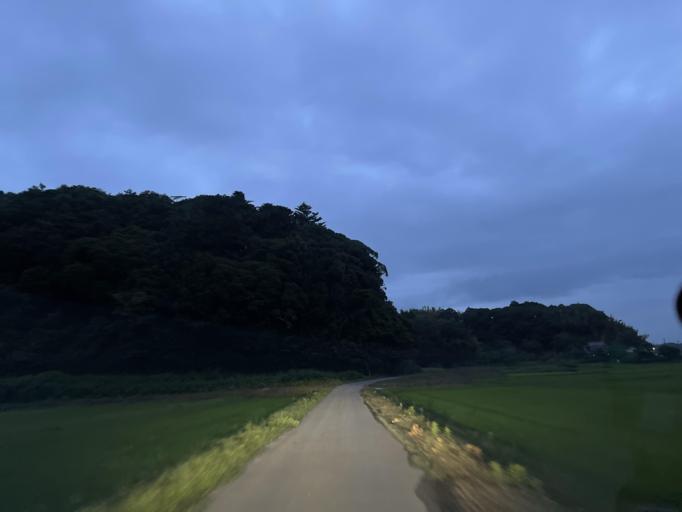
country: JP
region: Chiba
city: Omigawa
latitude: 35.7935
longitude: 140.6154
